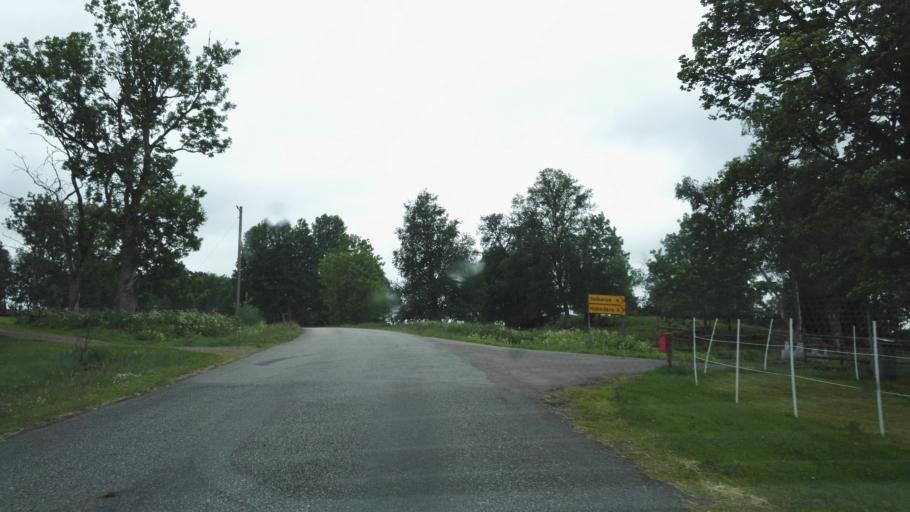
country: SE
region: Joenkoeping
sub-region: Vetlanda Kommun
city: Landsbro
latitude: 57.2870
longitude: 14.8315
